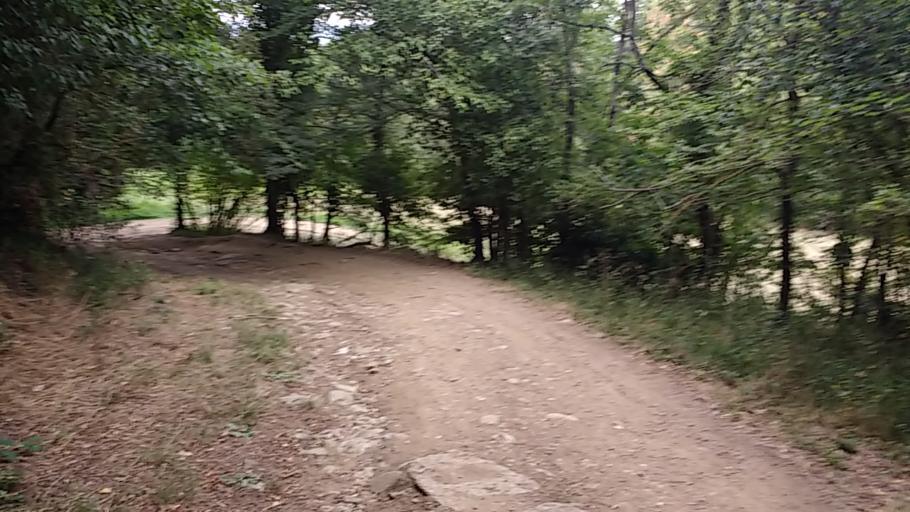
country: FR
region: Languedoc-Roussillon
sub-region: Departement des Pyrenees-Orientales
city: Ria-Sirach
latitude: 42.5942
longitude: 2.4156
